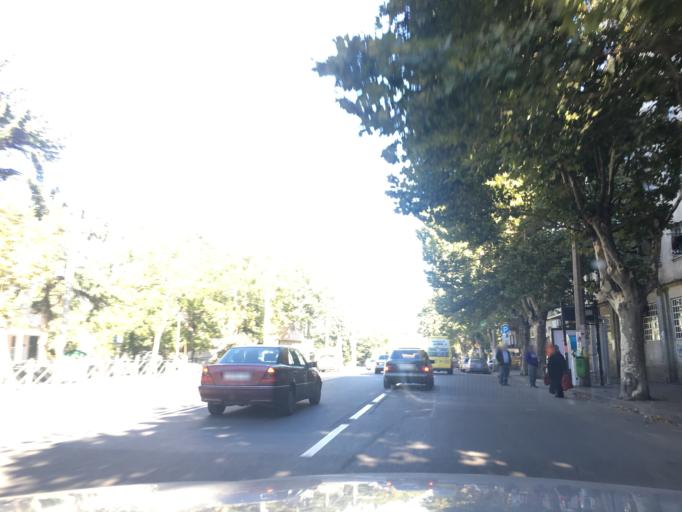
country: GE
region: T'bilisi
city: Tbilisi
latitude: 41.7458
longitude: 44.7925
